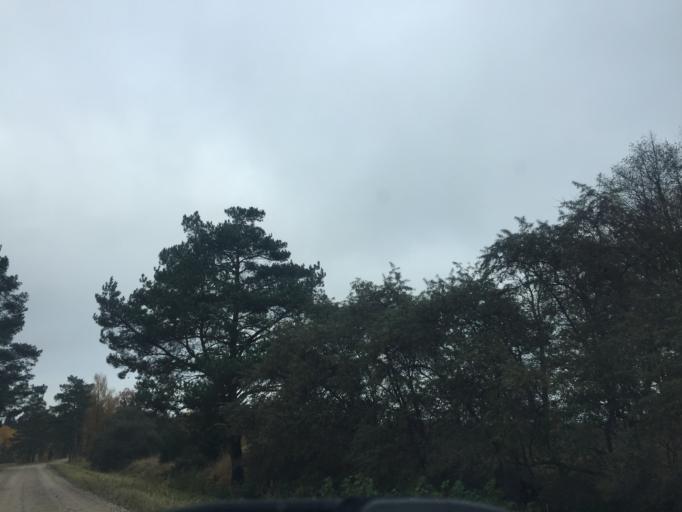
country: LV
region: Jaunpils
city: Jaunpils
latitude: 56.6923
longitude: 23.1163
